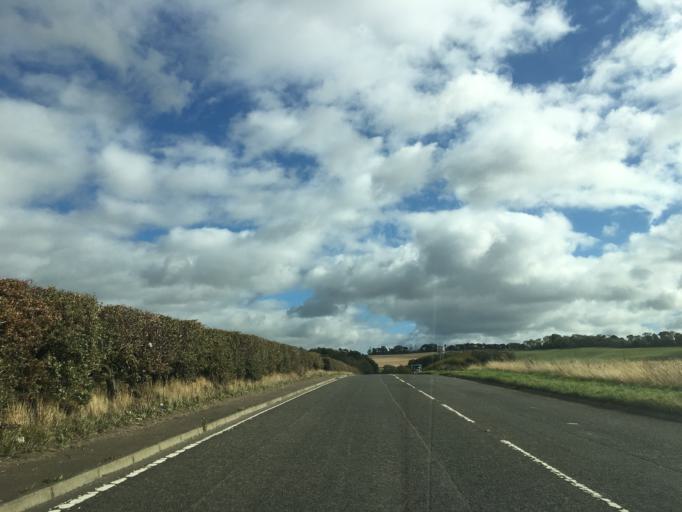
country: GB
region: Scotland
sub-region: Midlothian
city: Dalkeith
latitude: 55.8912
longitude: -3.0322
